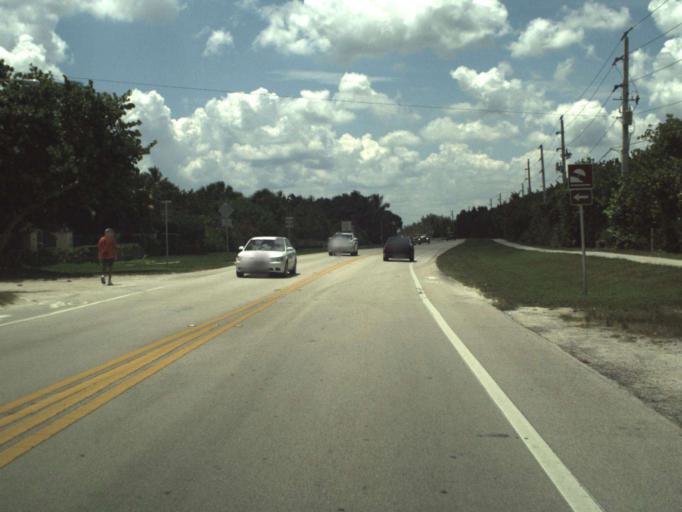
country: US
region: Florida
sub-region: Martin County
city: Jensen Beach
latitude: 27.2630
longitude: -80.2012
